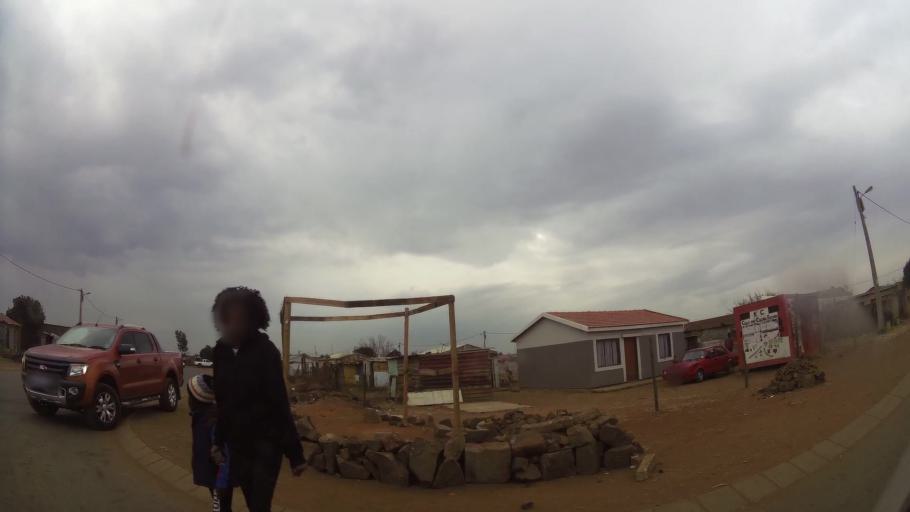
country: ZA
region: Gauteng
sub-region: Ekurhuleni Metropolitan Municipality
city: Germiston
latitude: -26.3867
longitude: 28.1377
